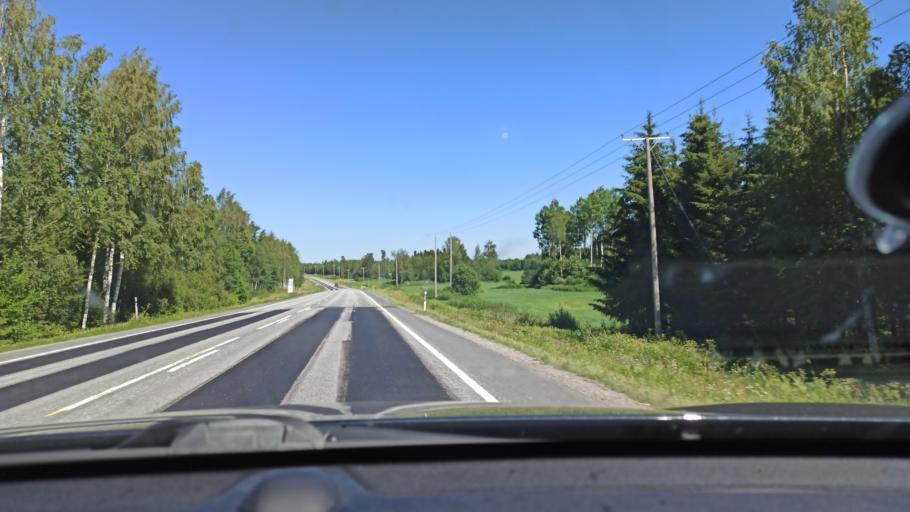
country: FI
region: Ostrobothnia
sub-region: Vaasa
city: Voera
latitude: 63.2137
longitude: 22.1947
